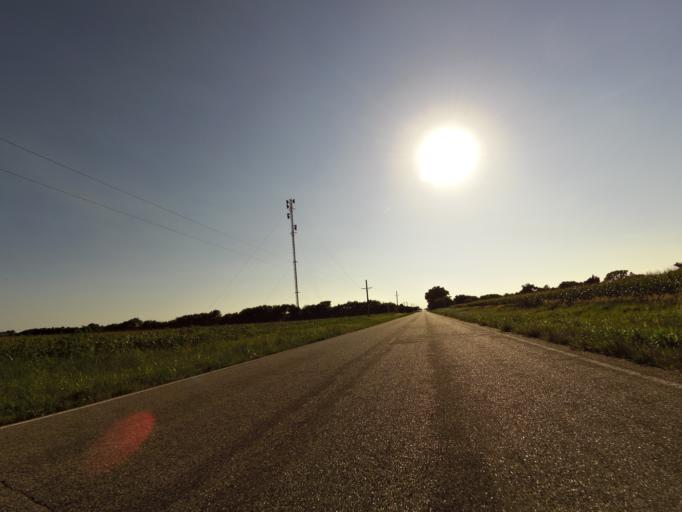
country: US
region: Kansas
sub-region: McPherson County
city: Moundridge
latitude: 38.1451
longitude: -97.5812
